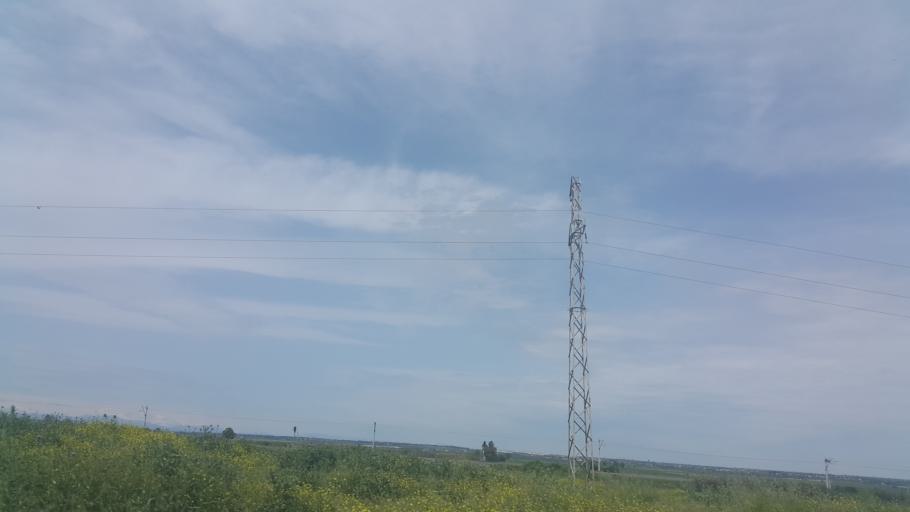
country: TR
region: Adana
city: Yuregir
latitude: 36.9778
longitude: 35.4695
